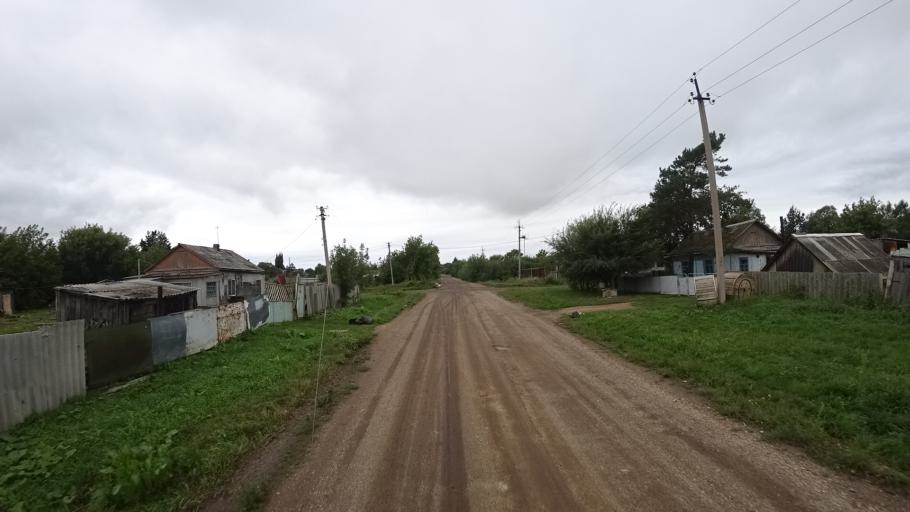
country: RU
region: Primorskiy
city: Chernigovka
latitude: 44.3424
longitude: 132.5479
